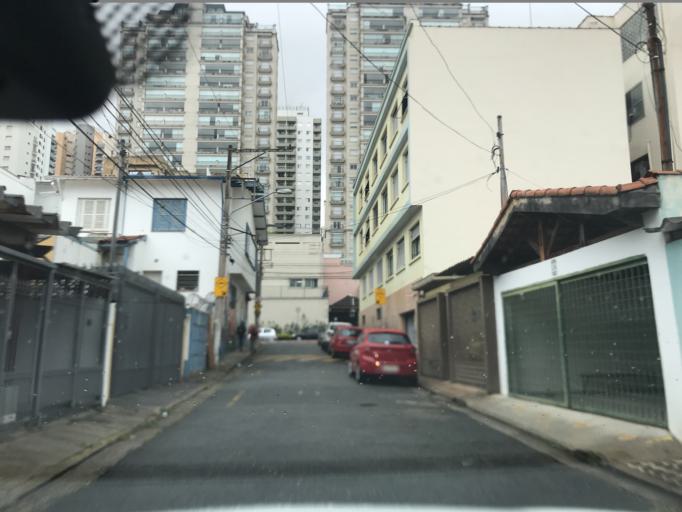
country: BR
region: Sao Paulo
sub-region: Sao Paulo
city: Sao Paulo
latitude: -23.5318
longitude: -46.6782
